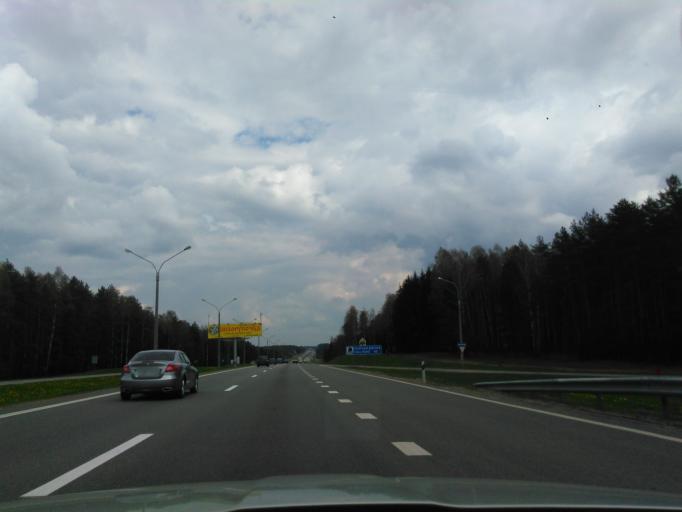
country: BY
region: Minsk
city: Kalodzishchy
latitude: 53.9695
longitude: 27.7509
